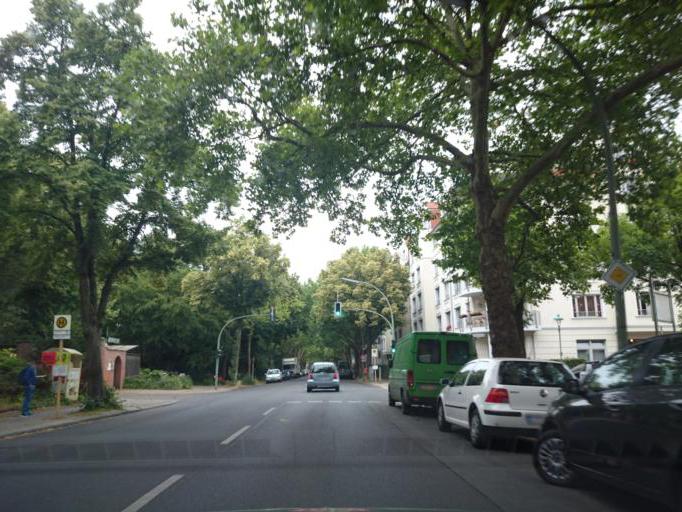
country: DE
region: Berlin
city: Schoneberg Bezirk
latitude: 52.4588
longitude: 13.3428
